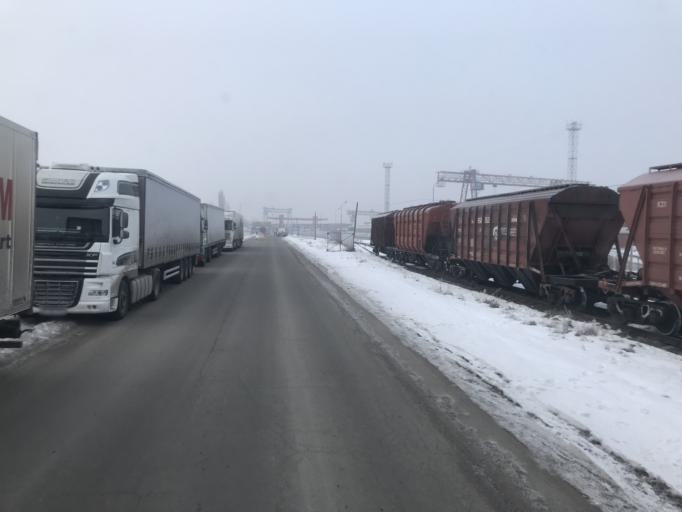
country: KZ
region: Almaty Oblysy
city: Pervomayskiy
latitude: 43.3601
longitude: 76.9762
